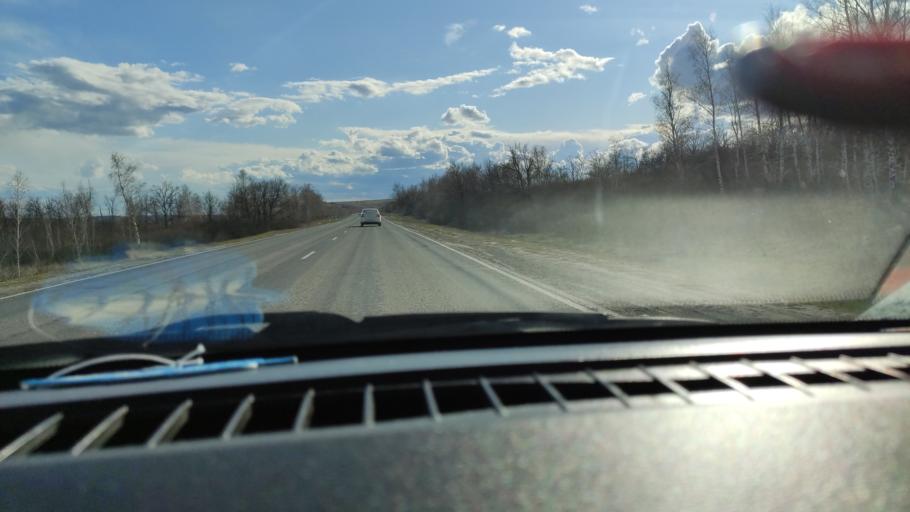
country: RU
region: Saratov
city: Sennoy
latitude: 52.1100
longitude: 46.8282
